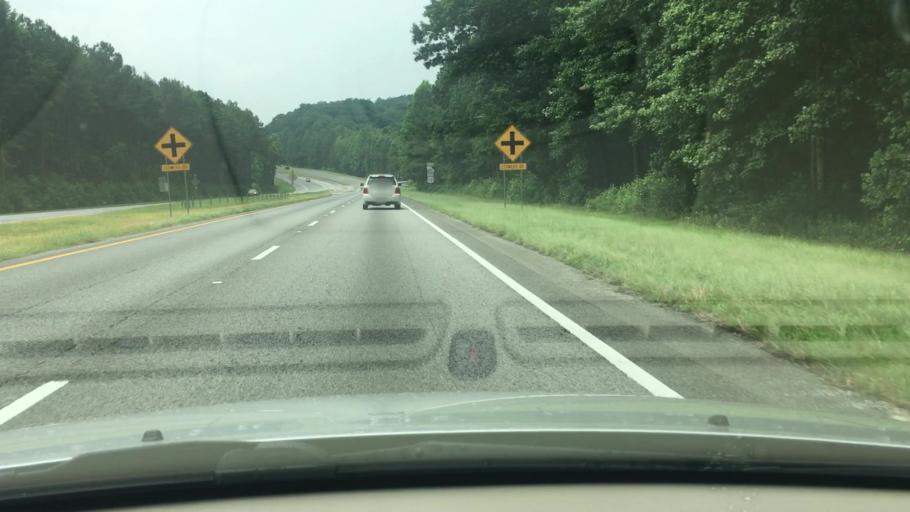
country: US
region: Georgia
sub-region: Dawson County
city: Dawsonville
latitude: 34.3980
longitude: -84.0133
